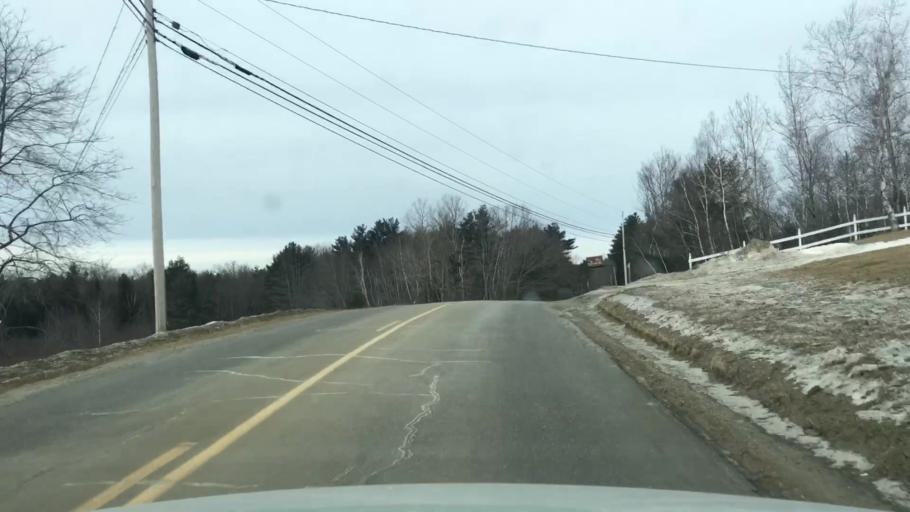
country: US
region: Maine
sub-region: Kennebec County
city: Chelsea
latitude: 44.2662
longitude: -69.6501
